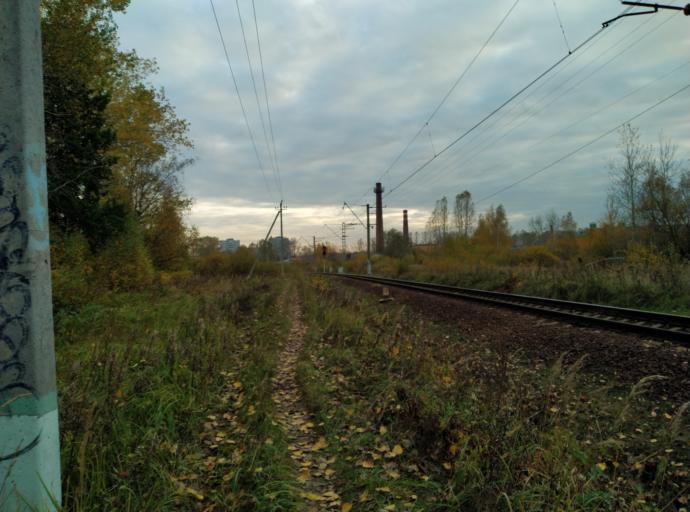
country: RU
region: Moskovskaya
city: Bol'shiye Vyazemy
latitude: 55.6186
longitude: 36.9729
